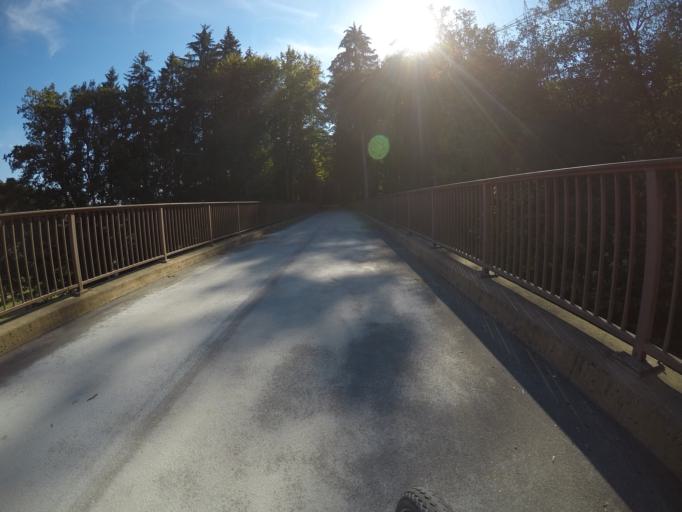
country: DE
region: Baden-Wuerttemberg
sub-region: Regierungsbezirk Stuttgart
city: Steinenbronn
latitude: 48.6818
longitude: 9.1260
